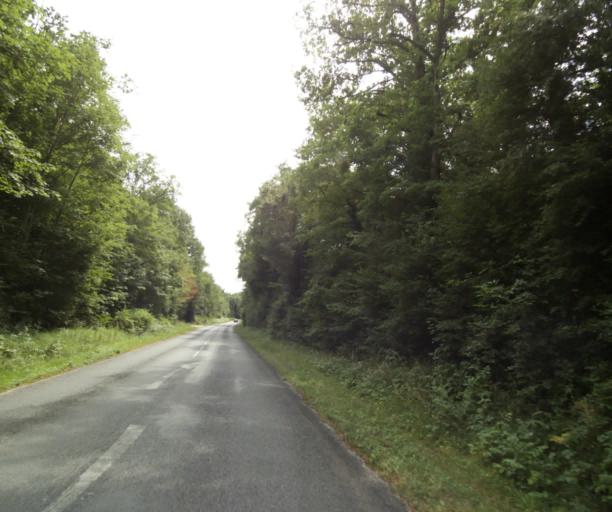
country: FR
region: Ile-de-France
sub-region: Departement de Seine-et-Marne
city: Chailly-en-Biere
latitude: 48.4866
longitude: 2.6284
